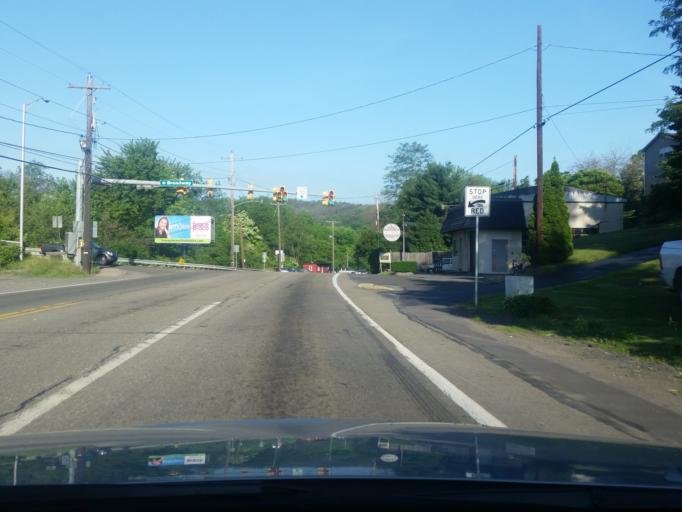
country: US
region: Pennsylvania
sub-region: Luzerne County
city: Nanticoke
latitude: 41.2164
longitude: -76.0027
